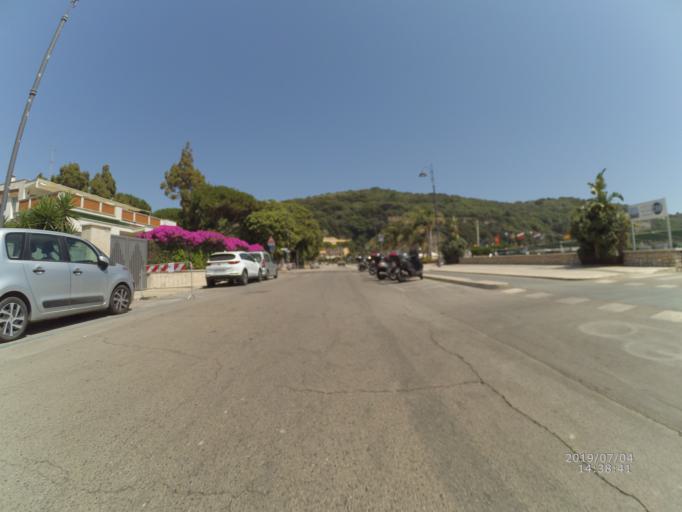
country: IT
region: Latium
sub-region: Provincia di Latina
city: Gaeta
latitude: 41.2100
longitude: 13.5691
